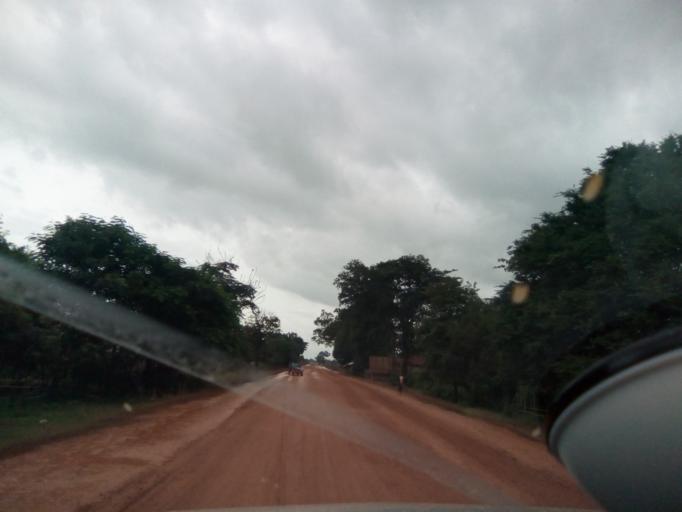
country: LA
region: Attapu
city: Attapu
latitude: 14.7624
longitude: 106.7136
